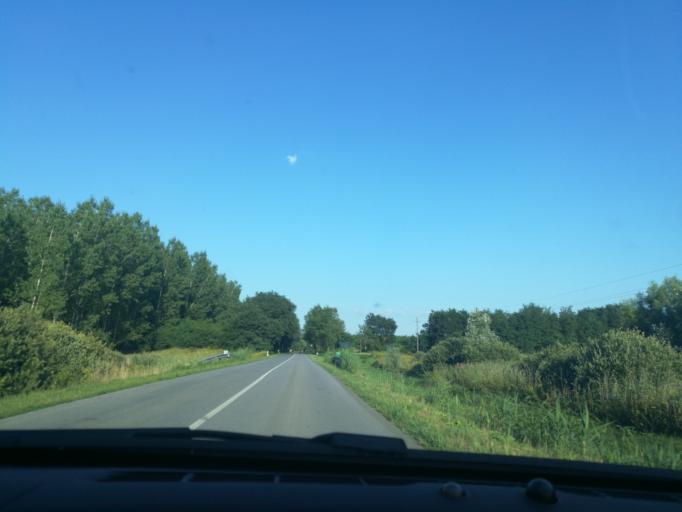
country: HU
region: Szabolcs-Szatmar-Bereg
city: Buj
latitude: 48.1201
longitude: 21.6504
